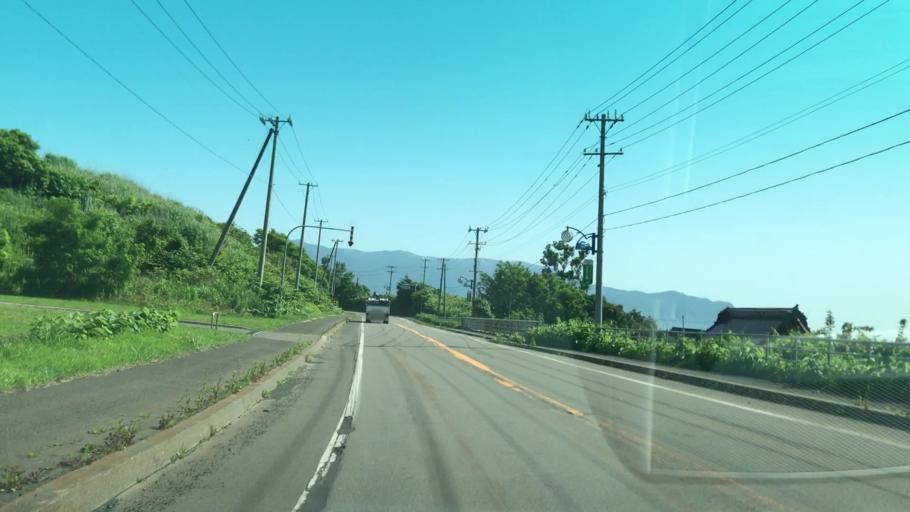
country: JP
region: Hokkaido
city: Iwanai
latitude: 43.0617
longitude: 140.4973
